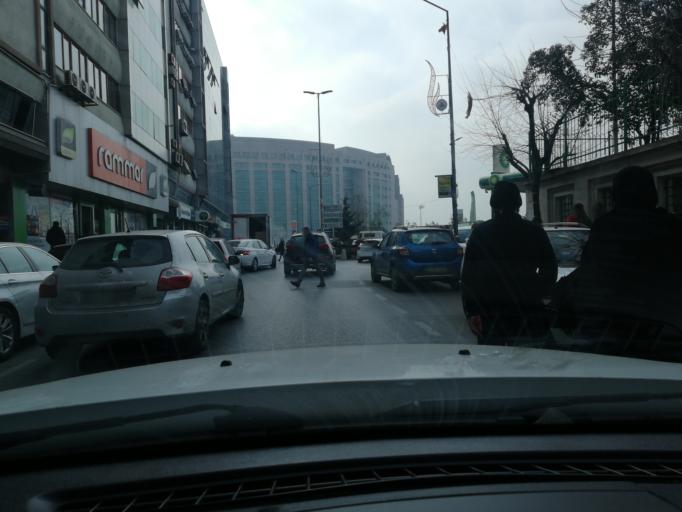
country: TR
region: Istanbul
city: Sisli
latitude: 41.0719
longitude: 28.9801
